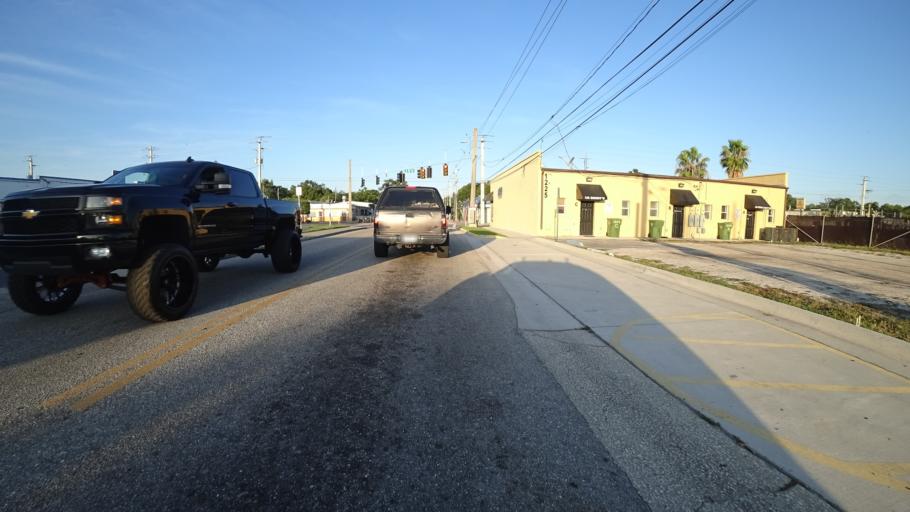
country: US
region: Florida
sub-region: Manatee County
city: Bradenton
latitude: 27.4881
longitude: -82.5707
